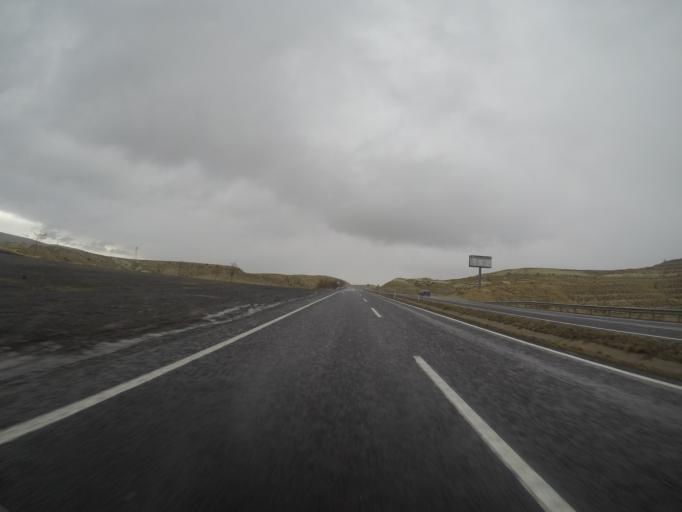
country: TR
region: Nevsehir
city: Urgub
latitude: 38.7401
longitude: 34.9992
